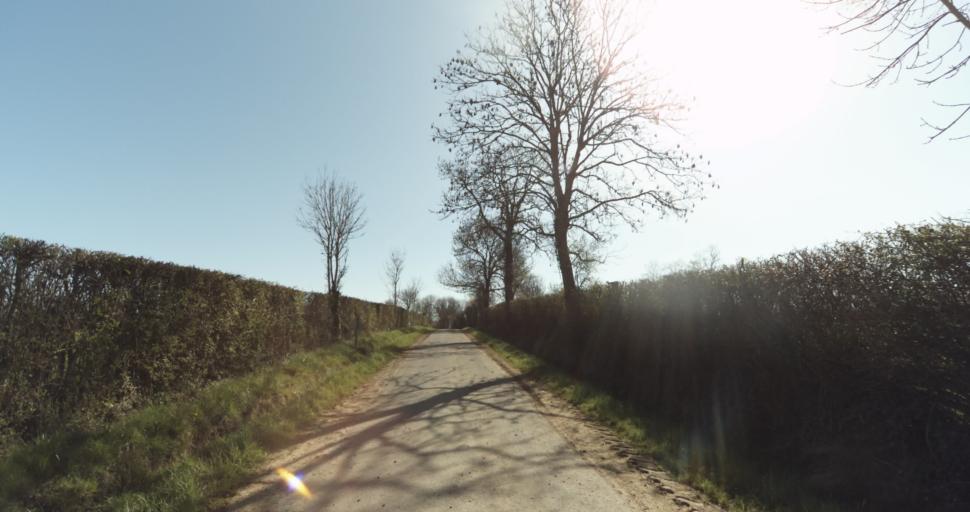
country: FR
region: Lower Normandy
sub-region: Departement du Calvados
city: Saint-Pierre-sur-Dives
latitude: 48.9683
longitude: 0.0005
